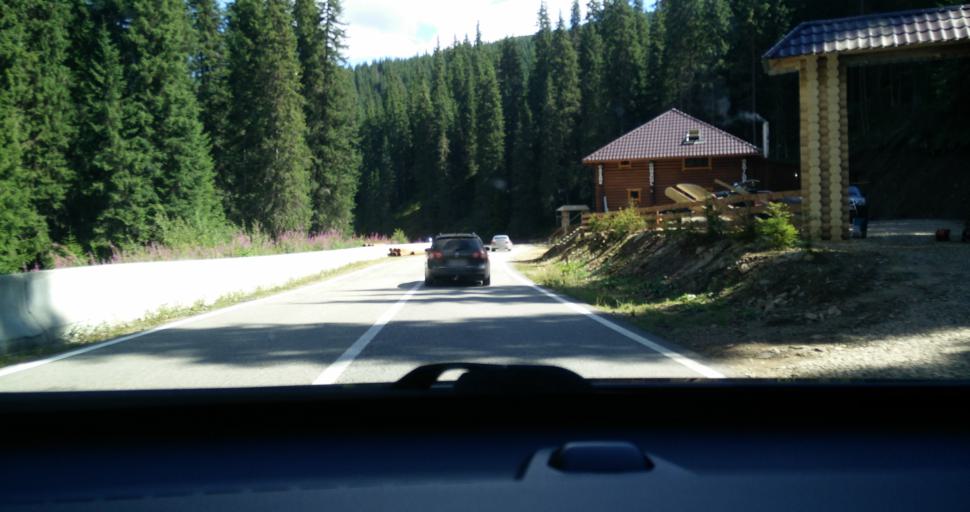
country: RO
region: Hunedoara
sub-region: Oras Petrila
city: Petrila
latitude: 45.5124
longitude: 23.6495
